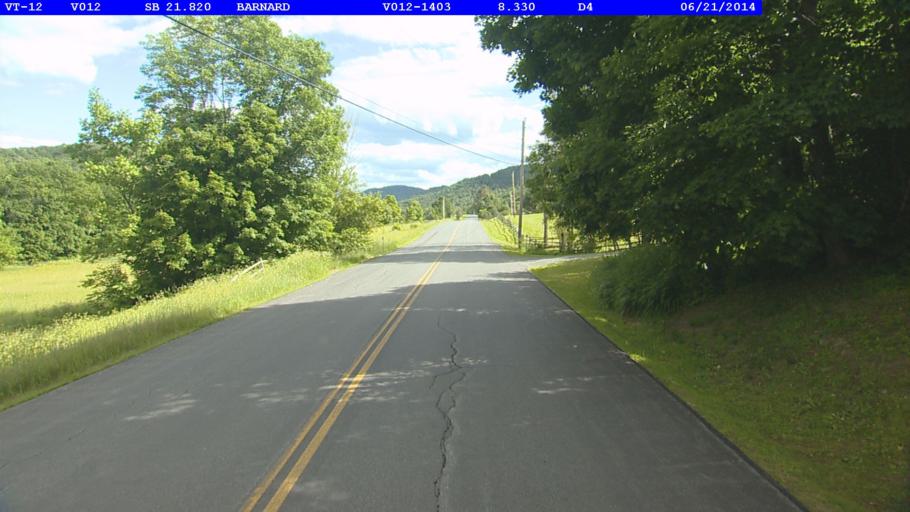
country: US
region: Vermont
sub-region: Orange County
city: Randolph
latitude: 43.7756
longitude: -72.6364
